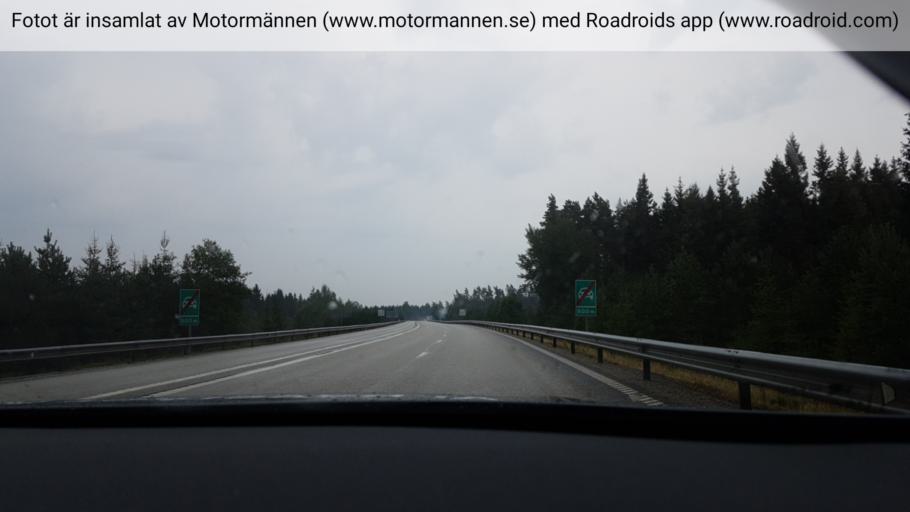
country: SE
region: Joenkoeping
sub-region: Jonkopings Kommun
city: Odensjo
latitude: 57.6197
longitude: 14.1948
